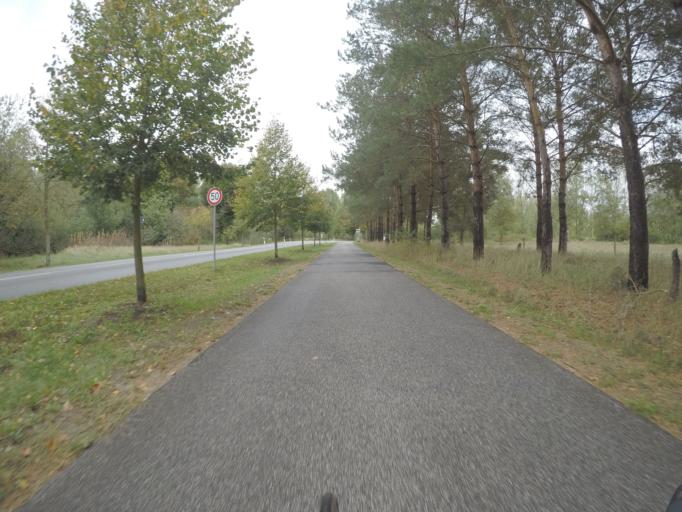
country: DE
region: Berlin
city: Buch
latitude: 52.6728
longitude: 13.4988
